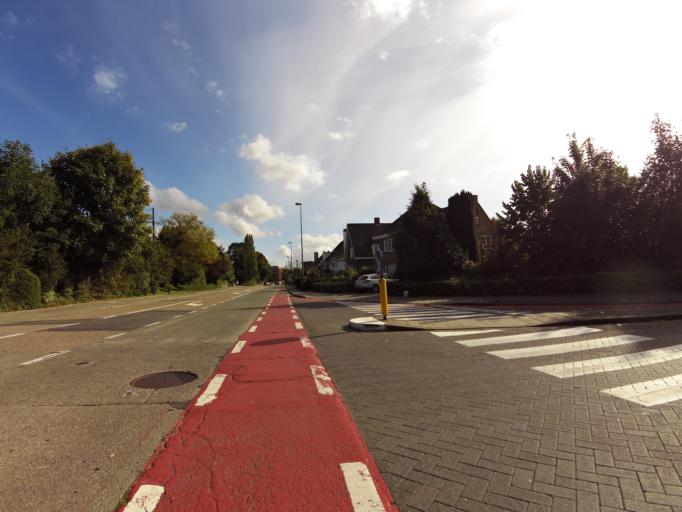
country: BE
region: Flanders
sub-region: Provincie West-Vlaanderen
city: Brugge
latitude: 51.2019
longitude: 3.2114
